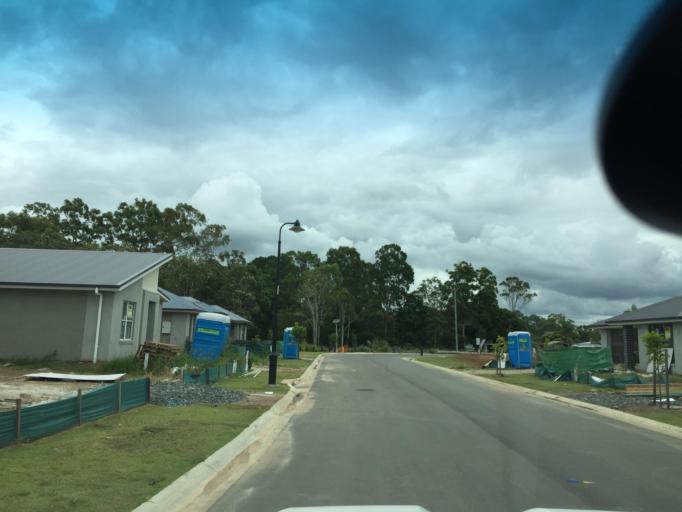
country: AU
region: Queensland
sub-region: Moreton Bay
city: Caboolture
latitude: -27.0652
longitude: 152.9226
